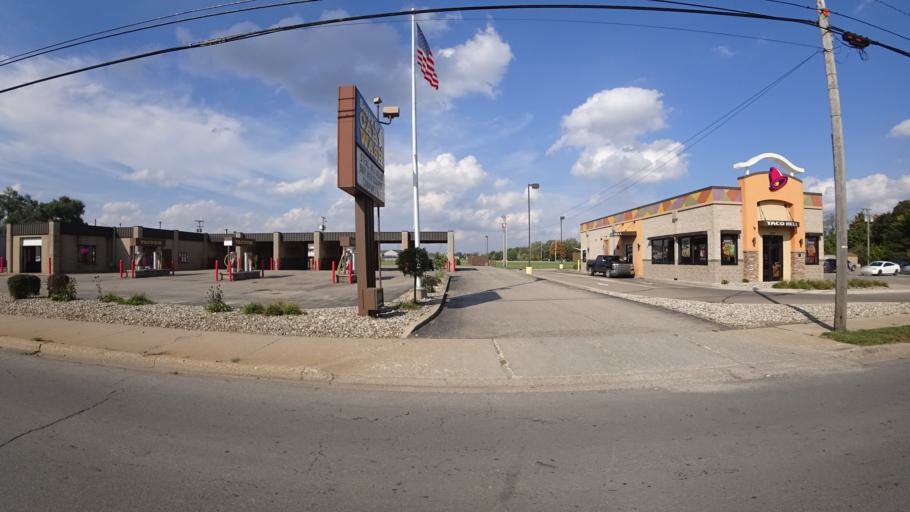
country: US
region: Michigan
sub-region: Saint Joseph County
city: Three Rivers
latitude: 41.9426
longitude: -85.6463
